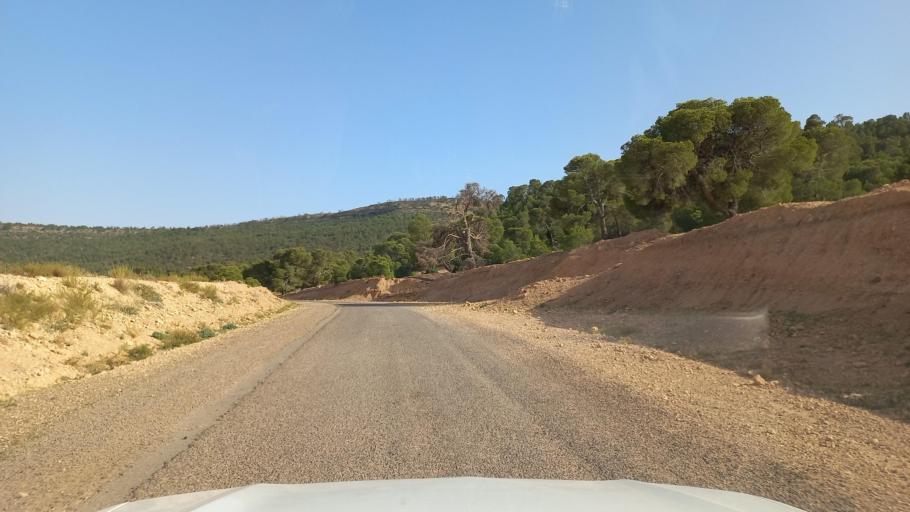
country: TN
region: Al Qasrayn
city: Kasserine
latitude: 35.3338
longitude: 8.8411
